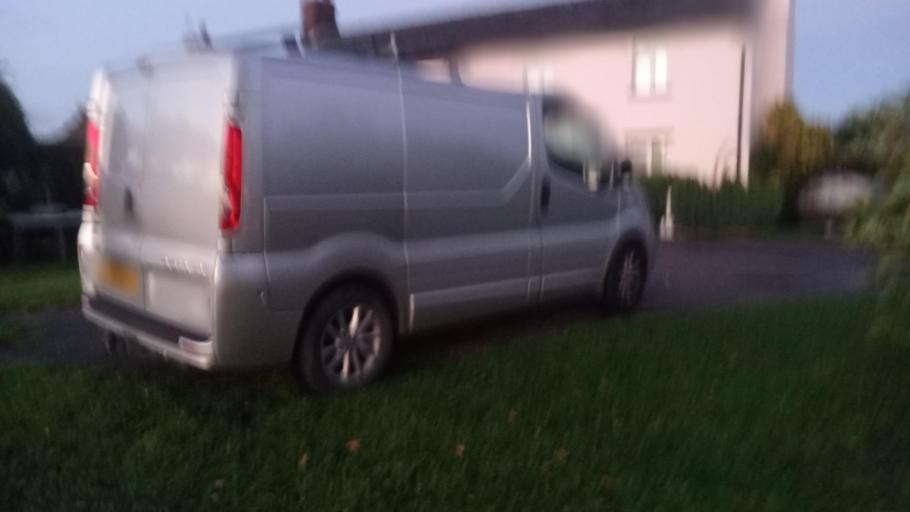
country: GB
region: England
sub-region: Cambridgeshire
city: Linton
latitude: 52.0578
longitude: 0.3257
